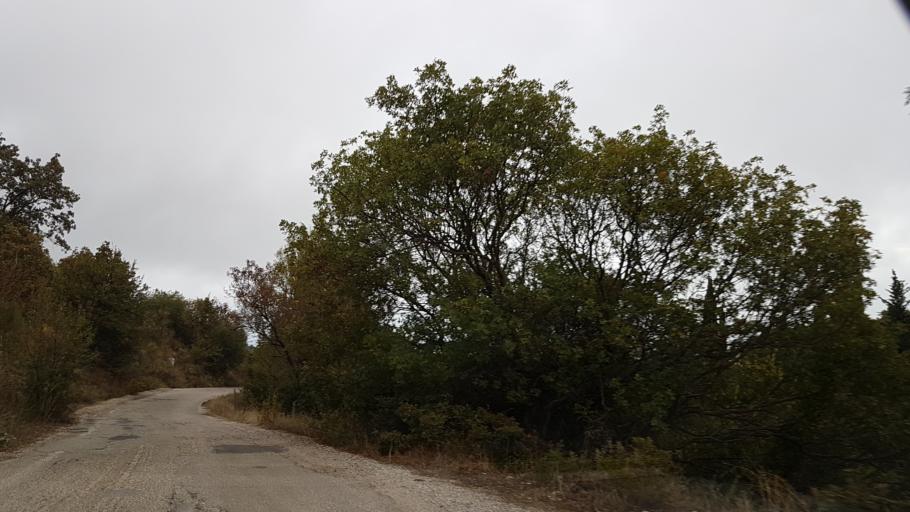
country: GR
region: Ionian Islands
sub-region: Nomos Kerkyras
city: Acharavi
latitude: 39.7799
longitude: 19.8823
